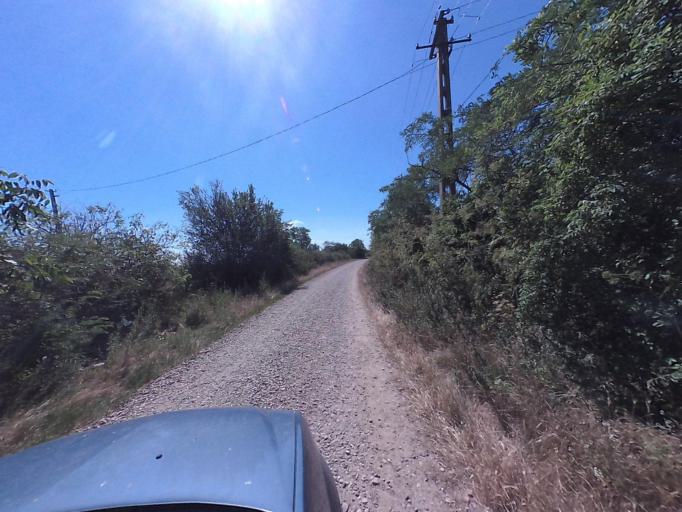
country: RO
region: Vaslui
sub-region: Comuna Costesti
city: Costesti
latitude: 46.4789
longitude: 27.7923
